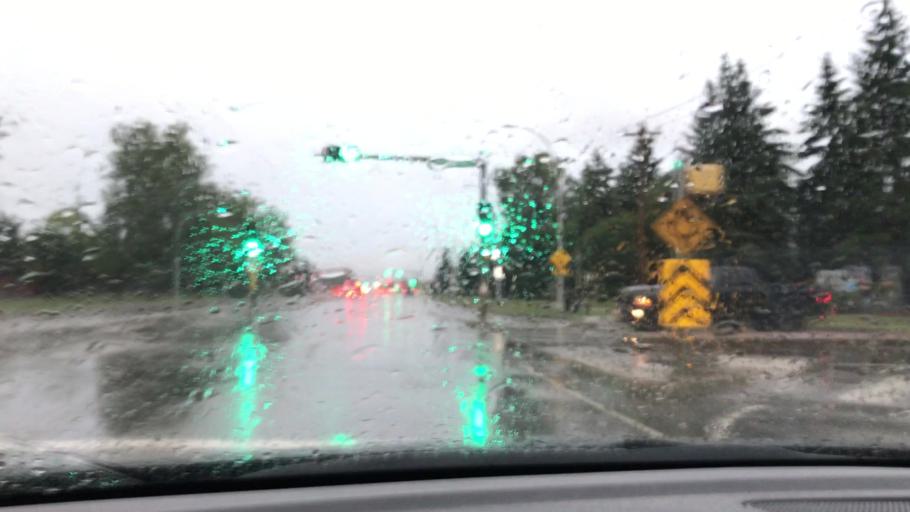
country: CA
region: Alberta
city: Sherwood Park
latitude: 53.5158
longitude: -113.3201
